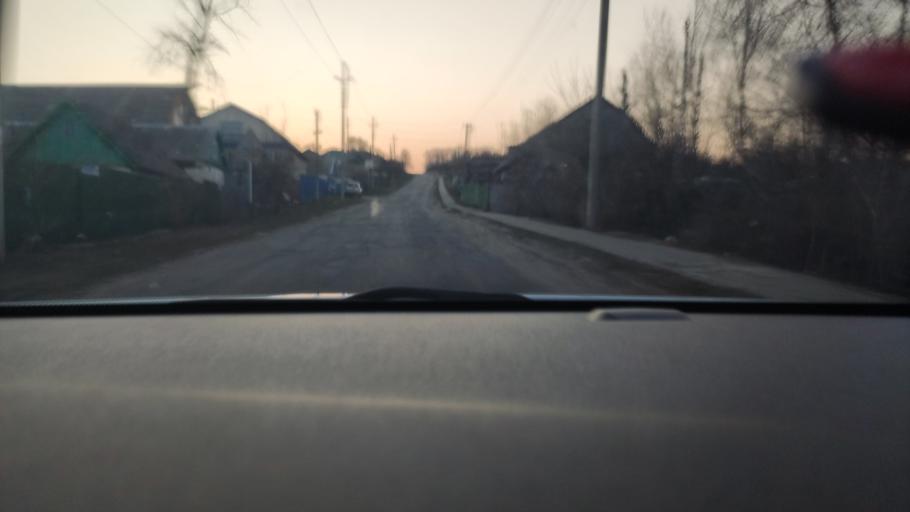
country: RU
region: Voronezj
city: Uryv-Pokrovka
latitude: 51.1123
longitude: 39.1539
